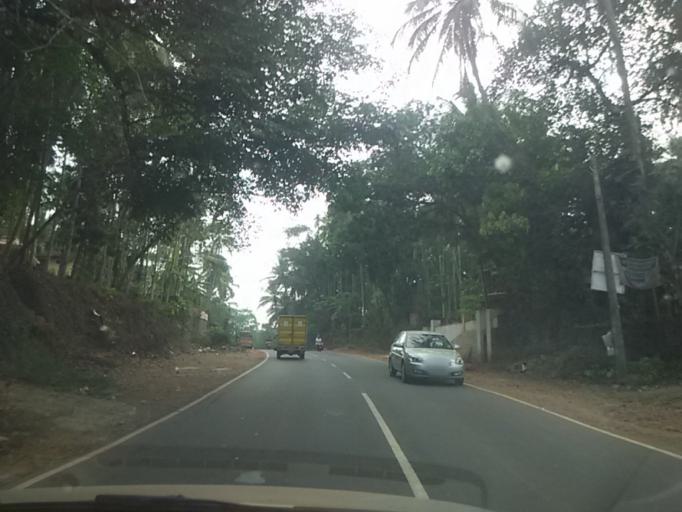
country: IN
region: Kerala
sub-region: Kozhikode
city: Naduvannur
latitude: 11.5316
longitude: 75.7724
